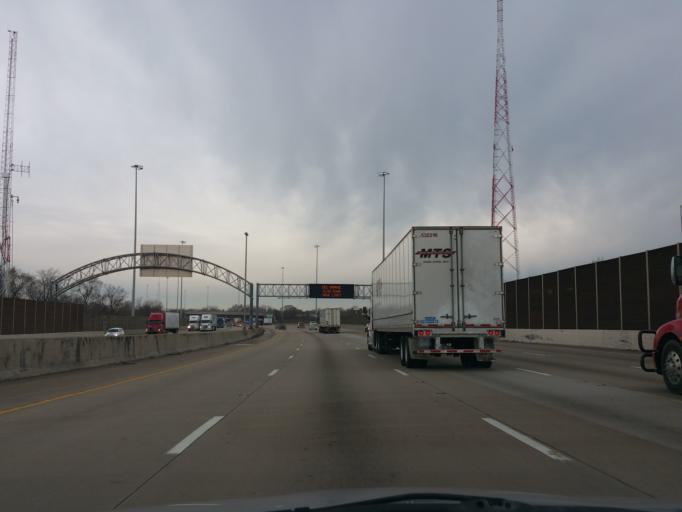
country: US
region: Indiana
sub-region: Lake County
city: Munster
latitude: 41.5768
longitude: -87.5239
